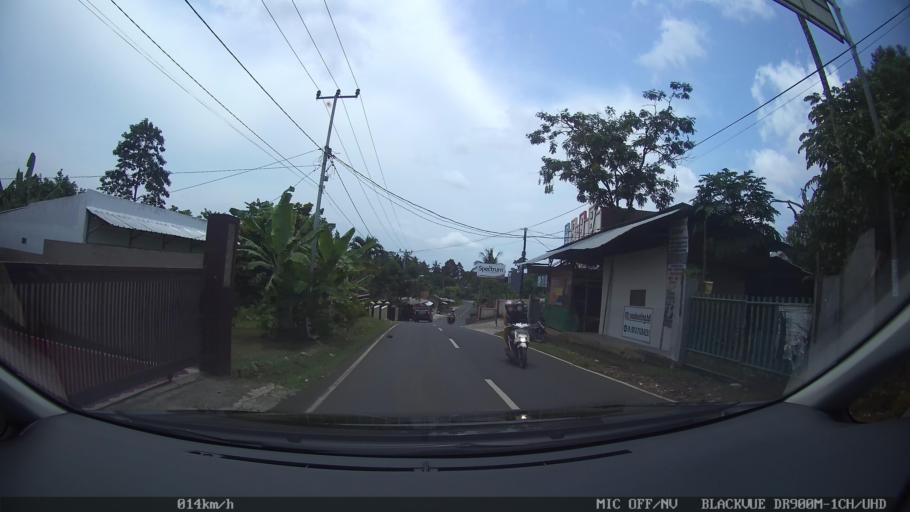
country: ID
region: Lampung
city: Bandarlampung
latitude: -5.4190
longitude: 105.2330
